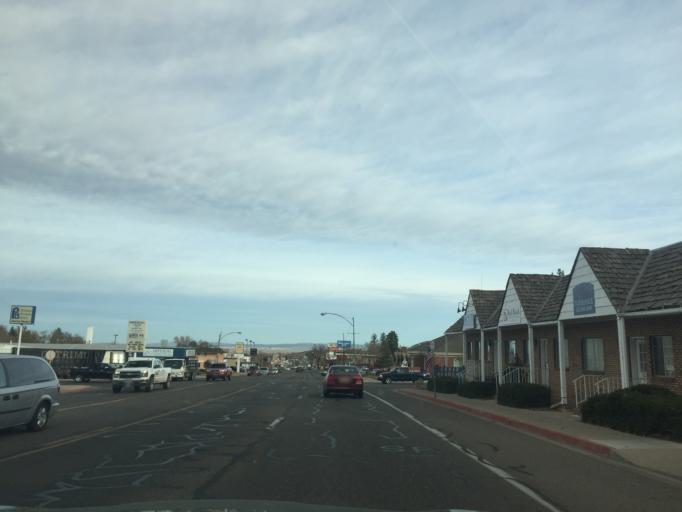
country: US
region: Utah
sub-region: Iron County
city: Cedar City
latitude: 37.6699
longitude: -113.0616
